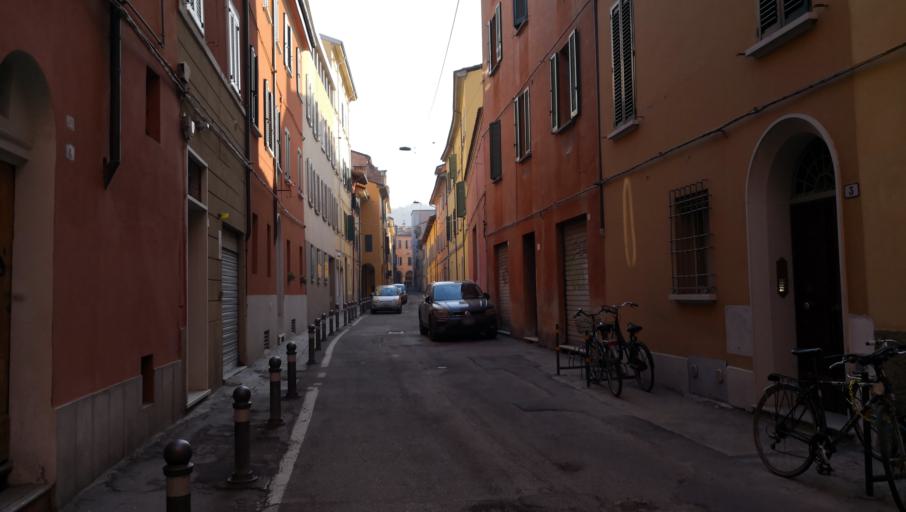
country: IT
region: Emilia-Romagna
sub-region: Provincia di Bologna
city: Bologna
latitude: 44.4919
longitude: 11.3359
